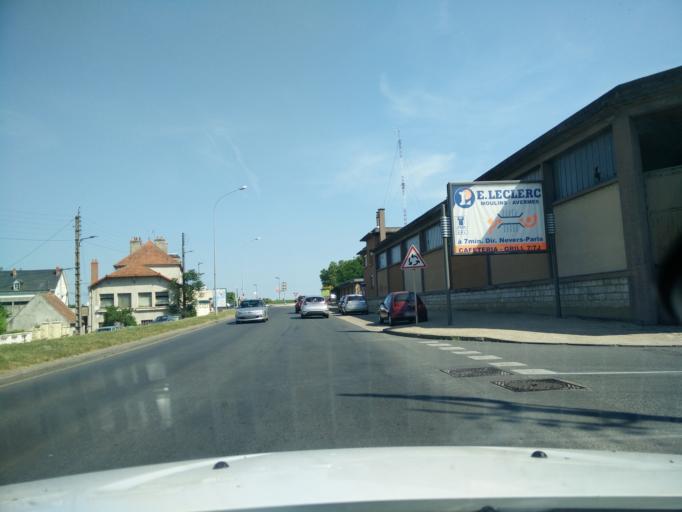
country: FR
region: Auvergne
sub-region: Departement de l'Allier
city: Moulins
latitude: 46.5599
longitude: 3.3213
